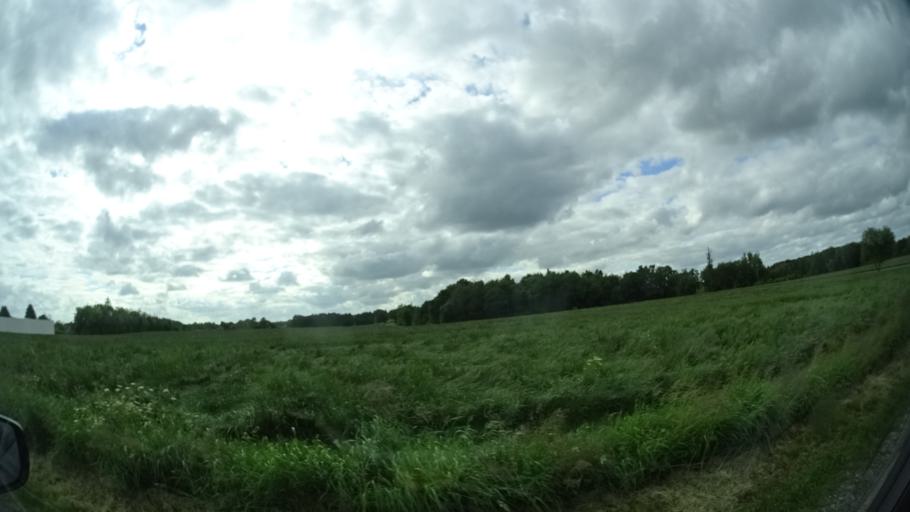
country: DK
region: Central Jutland
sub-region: Syddjurs Kommune
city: Ryomgard
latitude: 56.3894
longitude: 10.5123
